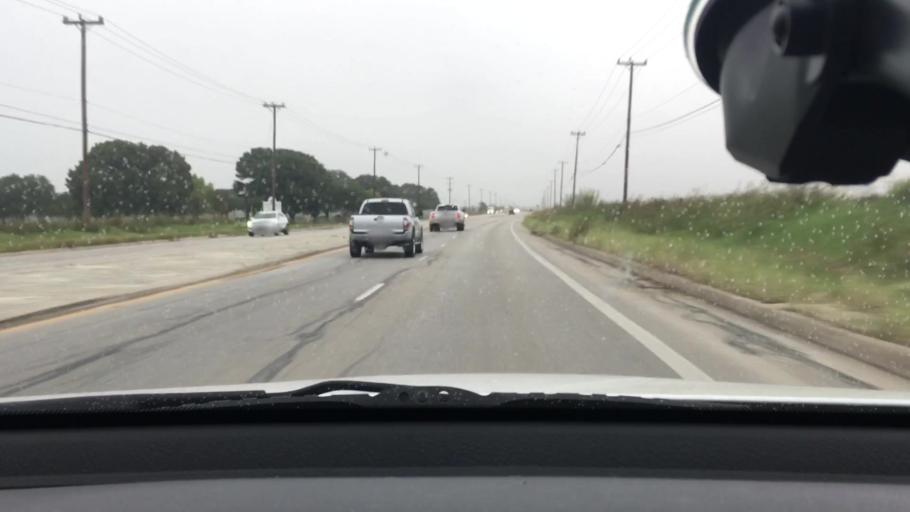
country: US
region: Texas
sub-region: Bexar County
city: Live Oak
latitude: 29.5985
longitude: -98.3390
